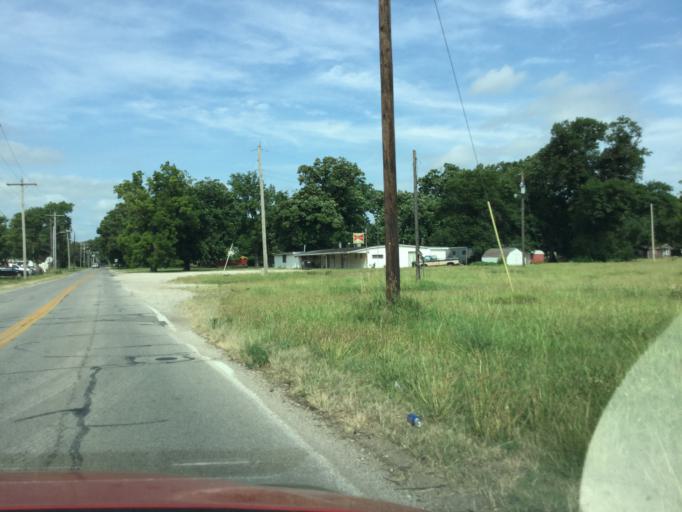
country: US
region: Kansas
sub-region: Shawnee County
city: Topeka
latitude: 39.0810
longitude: -95.6786
